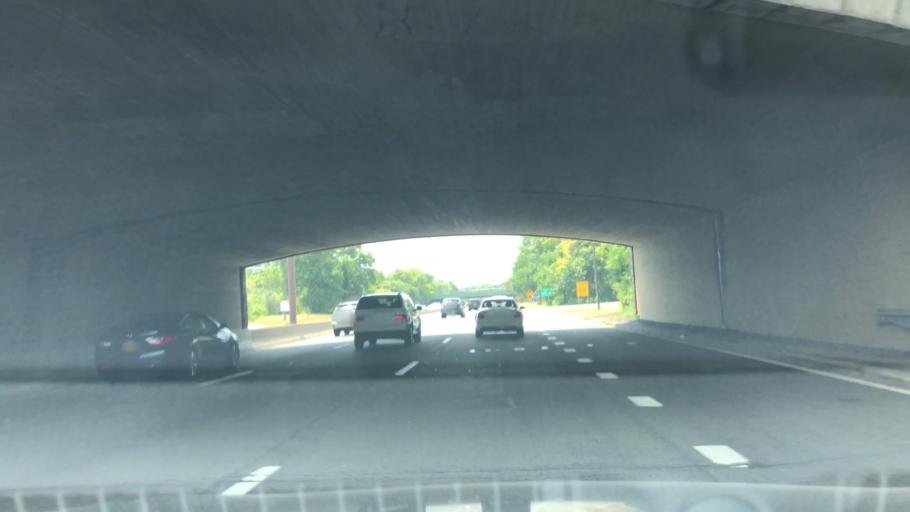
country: US
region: New York
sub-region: Nassau County
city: East Garden City
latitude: 40.7223
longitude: -73.5806
